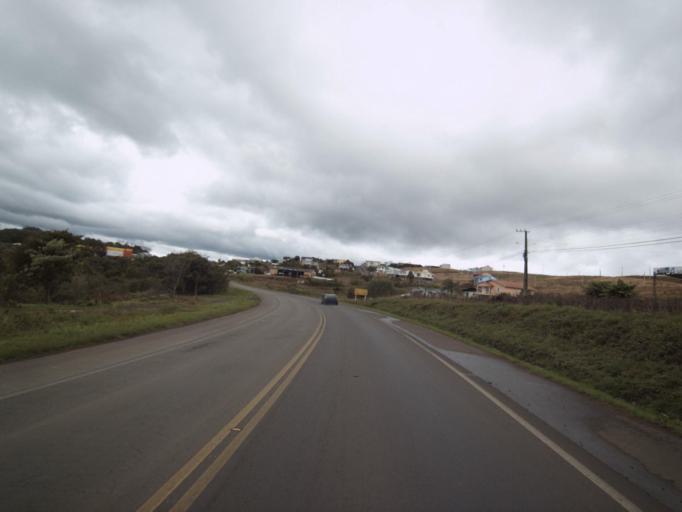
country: BR
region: Santa Catarina
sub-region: Concordia
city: Concordia
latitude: -27.2391
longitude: -51.9542
